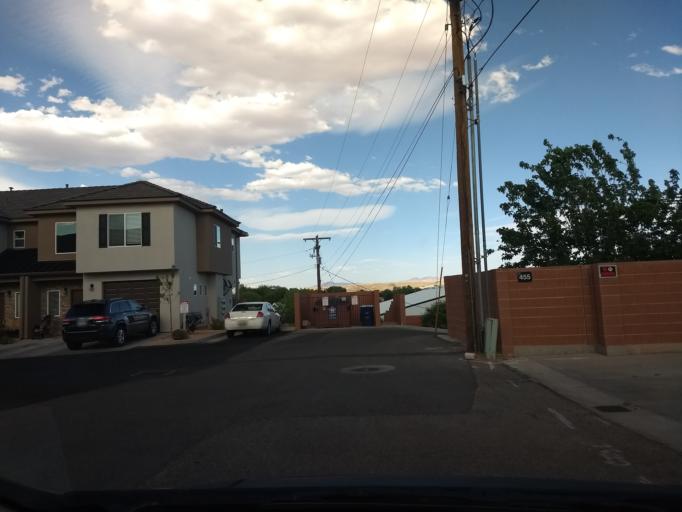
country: US
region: Utah
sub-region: Washington County
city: Washington
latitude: 37.1303
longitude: -113.5176
